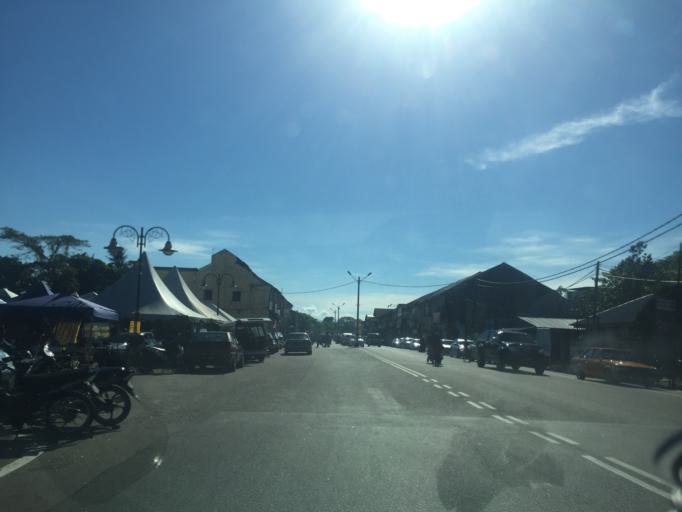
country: MY
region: Penang
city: Tasek Glugor
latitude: 5.5134
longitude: 100.5531
